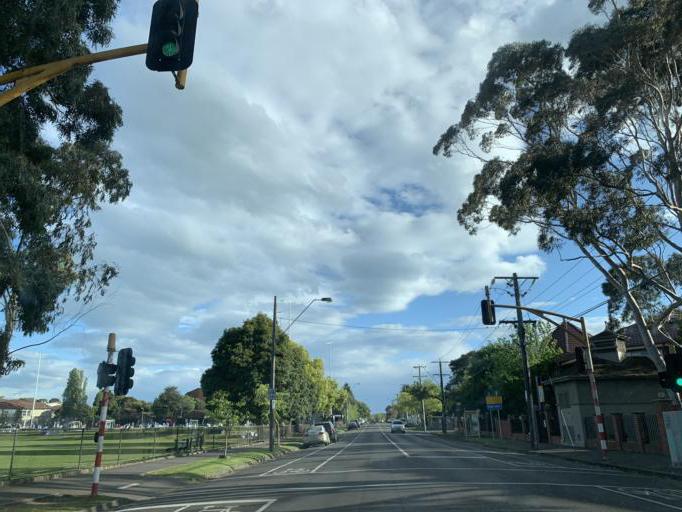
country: AU
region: Victoria
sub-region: Bayside
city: North Brighton
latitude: -37.9089
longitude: 144.9924
